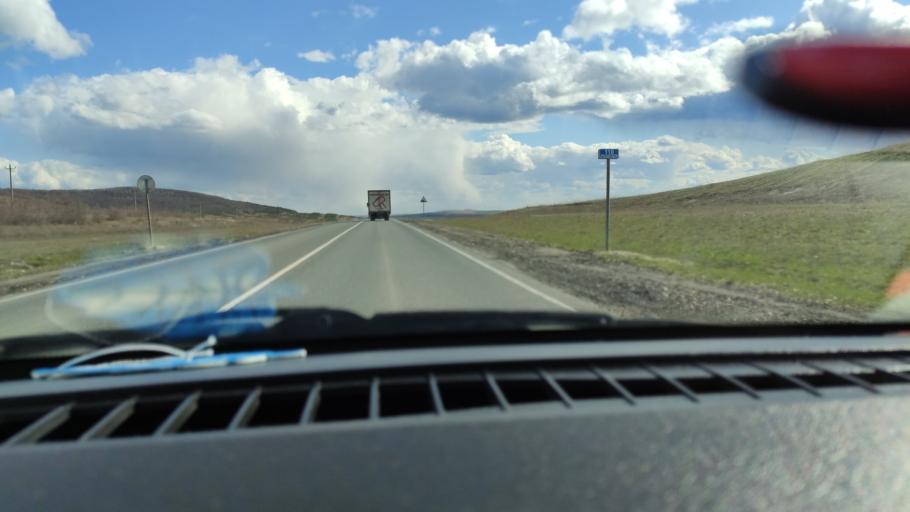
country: RU
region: Saratov
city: Alekseyevka
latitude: 52.3177
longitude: 47.9226
